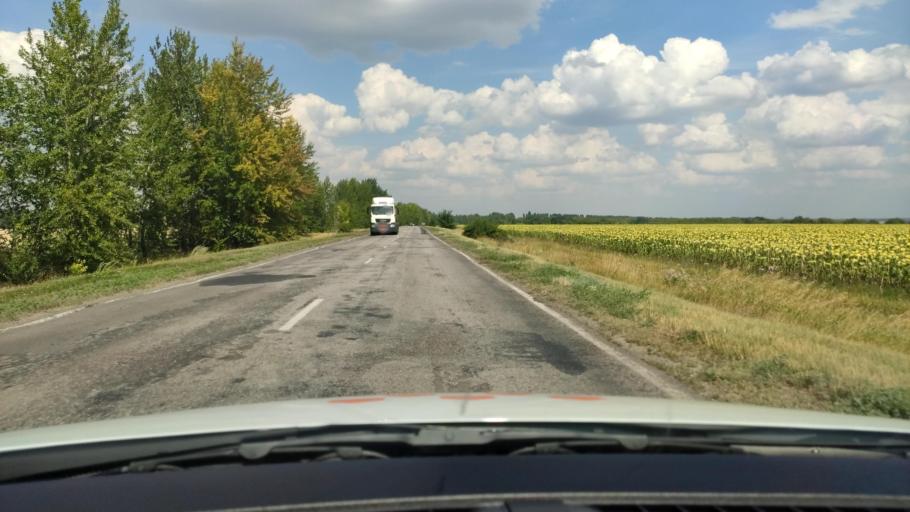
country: RU
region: Voronezj
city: Pereleshinskiy
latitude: 51.7510
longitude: 40.4159
